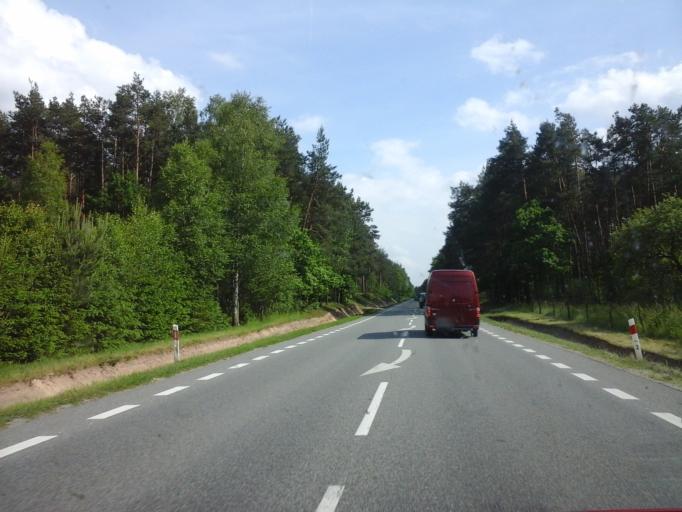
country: PL
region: Swietokrzyskie
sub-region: Powiat konecki
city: Ruda Maleniecka
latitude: 51.1758
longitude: 20.2208
